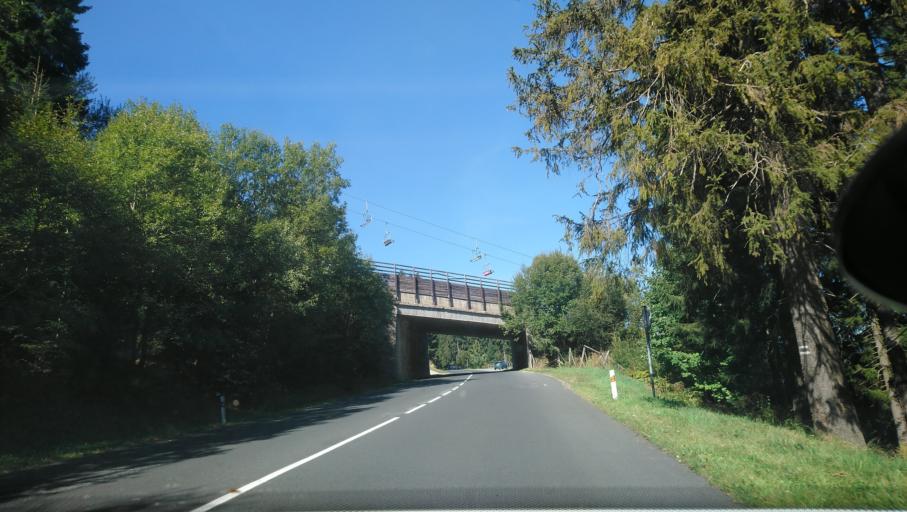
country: DE
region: Saxony
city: Kurort Oberwiesenthal
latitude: 50.4030
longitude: 12.9714
